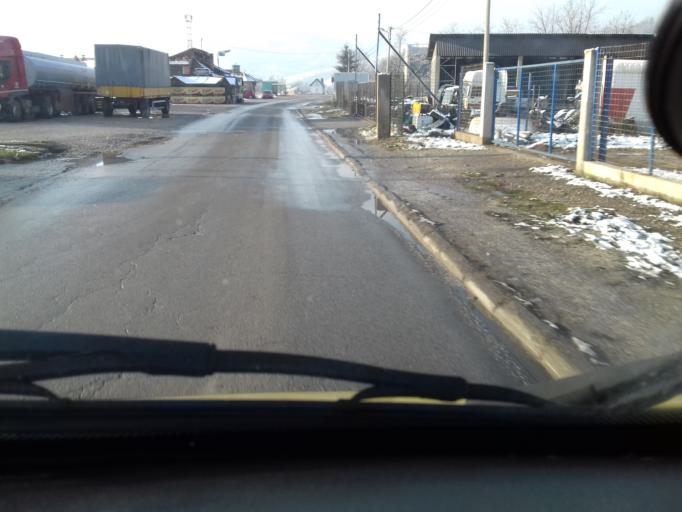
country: BA
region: Federation of Bosnia and Herzegovina
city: Mahala
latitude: 43.9897
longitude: 18.2302
